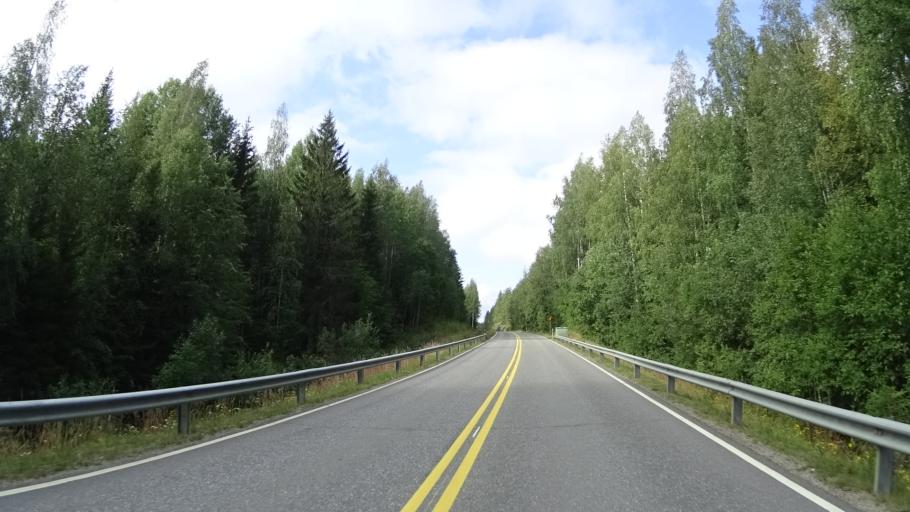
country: FI
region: Pirkanmaa
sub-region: Tampere
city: Luopioinen
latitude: 61.4946
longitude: 24.7837
